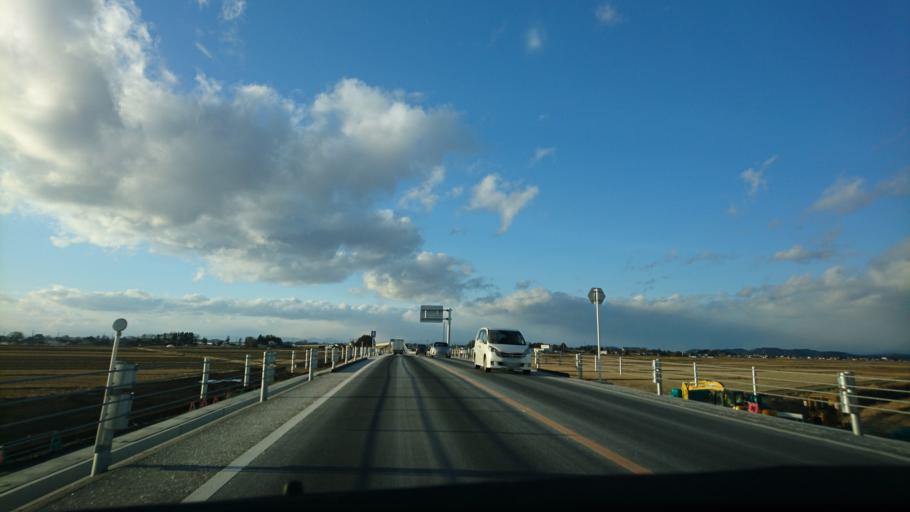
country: JP
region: Miyagi
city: Wakuya
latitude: 38.6799
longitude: 141.2565
